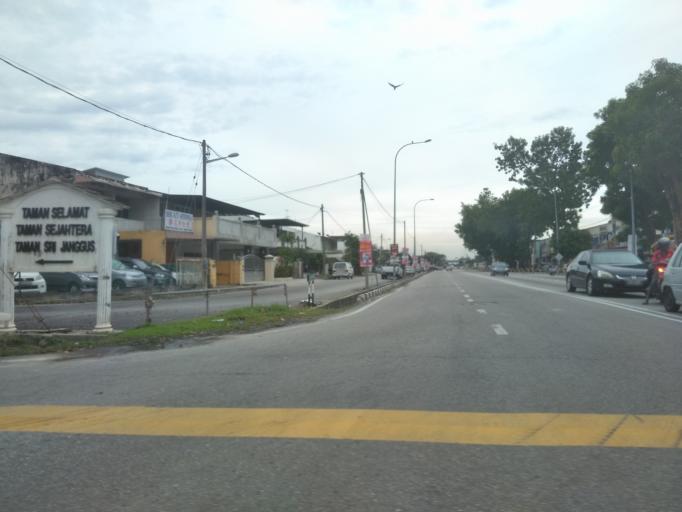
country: MY
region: Penang
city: Bukit Mertajam
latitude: 5.3333
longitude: 100.4816
